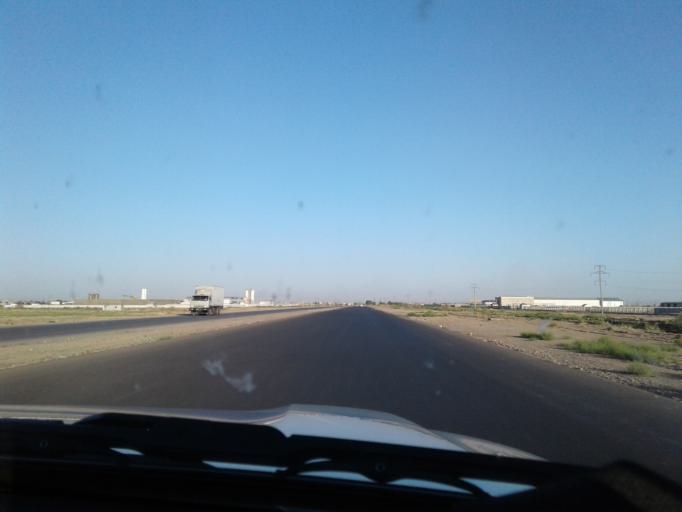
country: TM
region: Mary
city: Mary
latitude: 37.5787
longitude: 61.7961
